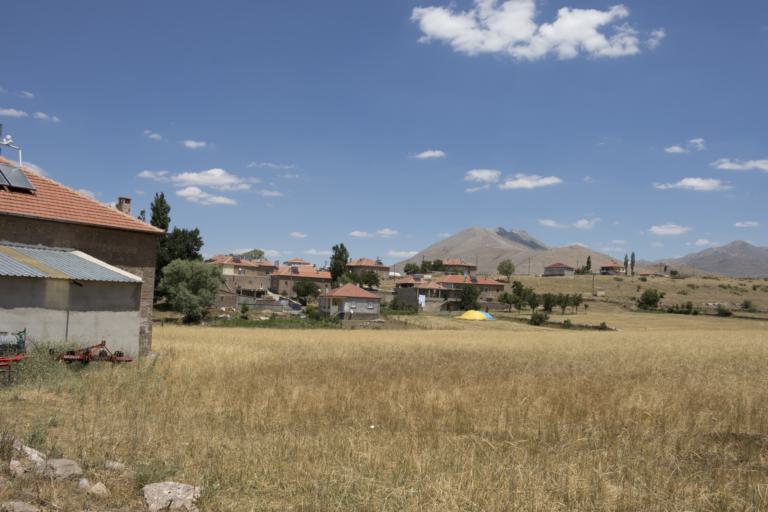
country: TR
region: Kayseri
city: Toklar
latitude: 38.4038
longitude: 36.0826
